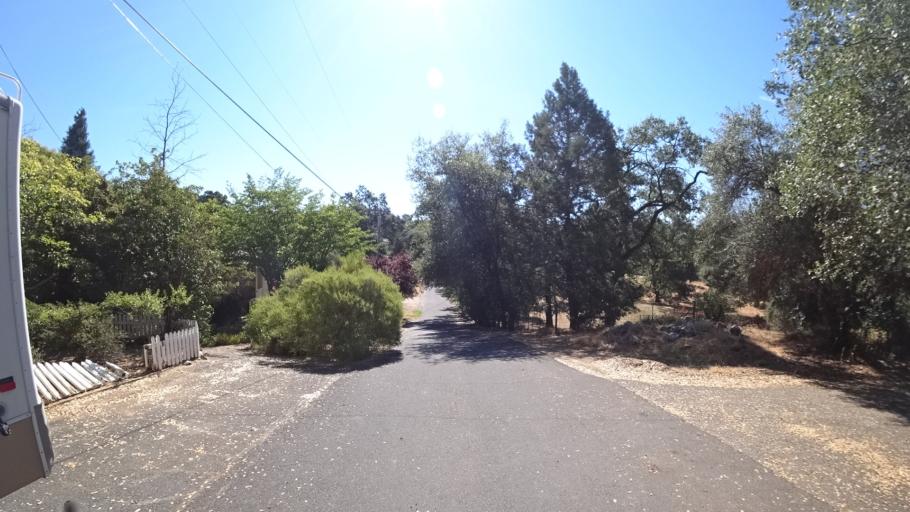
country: US
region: California
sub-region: Calaveras County
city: Angels Camp
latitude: 38.0742
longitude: -120.5569
